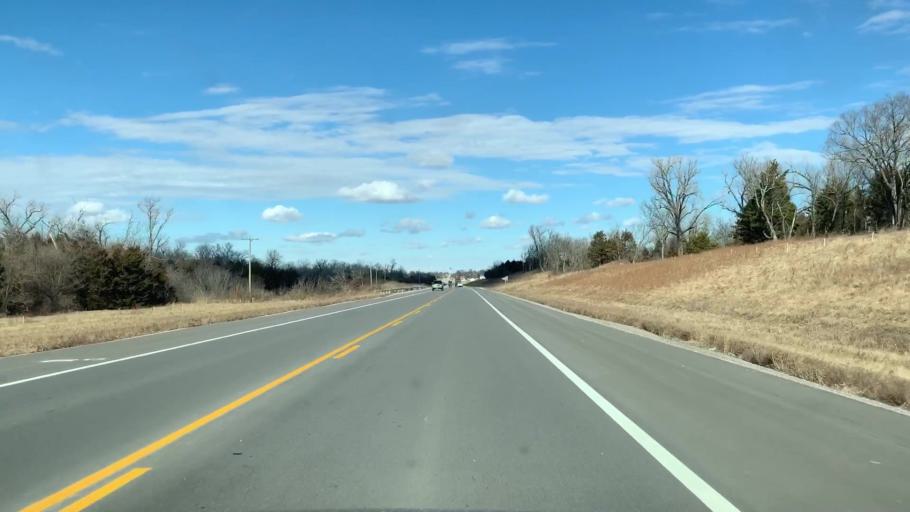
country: US
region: Kansas
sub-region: Crawford County
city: Pittsburg
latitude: 37.3268
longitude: -94.8322
